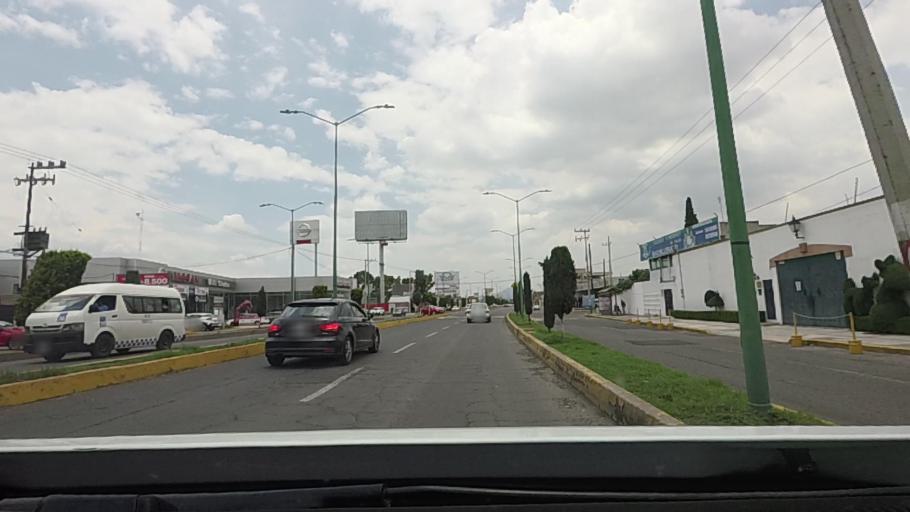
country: MX
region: Mexico
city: Chalco de Diaz Covarrubias
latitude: 19.2546
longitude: -98.8851
